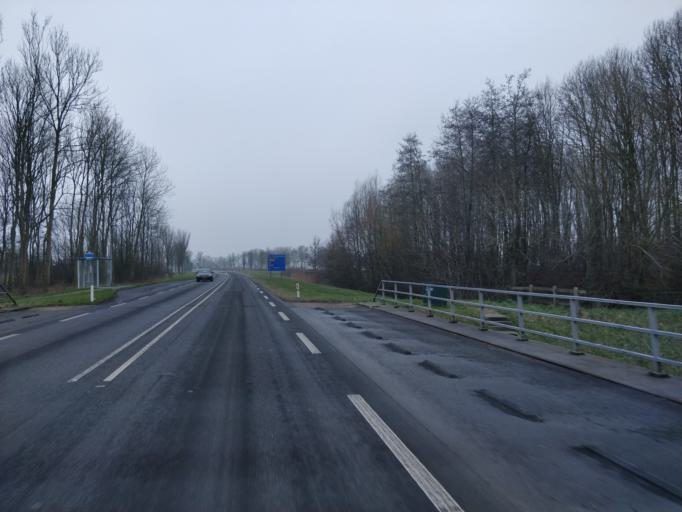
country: NL
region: Friesland
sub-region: Menameradiel
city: Menaam
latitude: 53.2367
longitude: 5.6817
